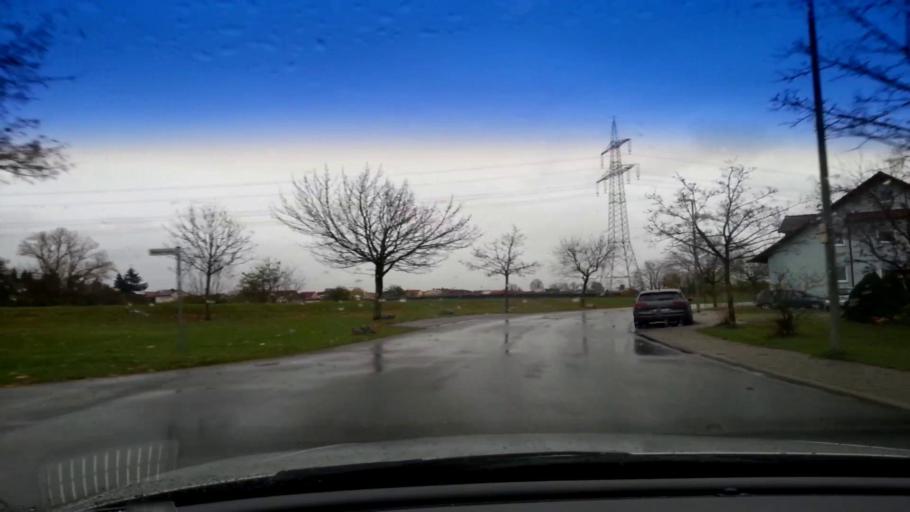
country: DE
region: Bavaria
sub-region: Upper Franconia
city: Hallstadt
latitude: 49.9325
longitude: 10.8649
